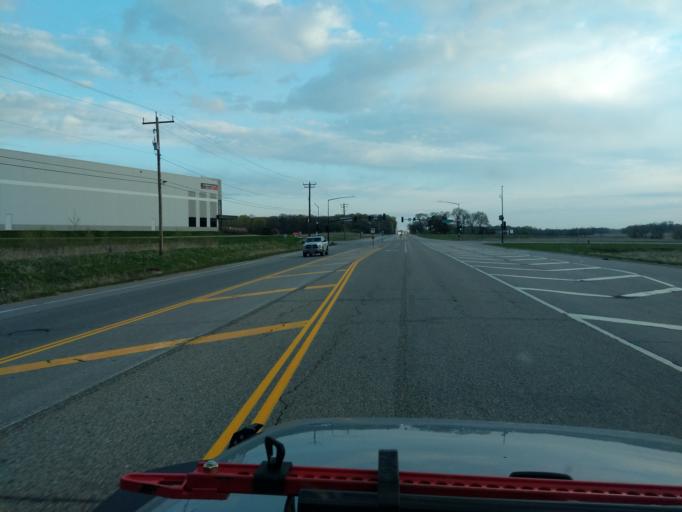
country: US
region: Minnesota
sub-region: Hennepin County
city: Rogers
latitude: 45.1816
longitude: -93.5231
